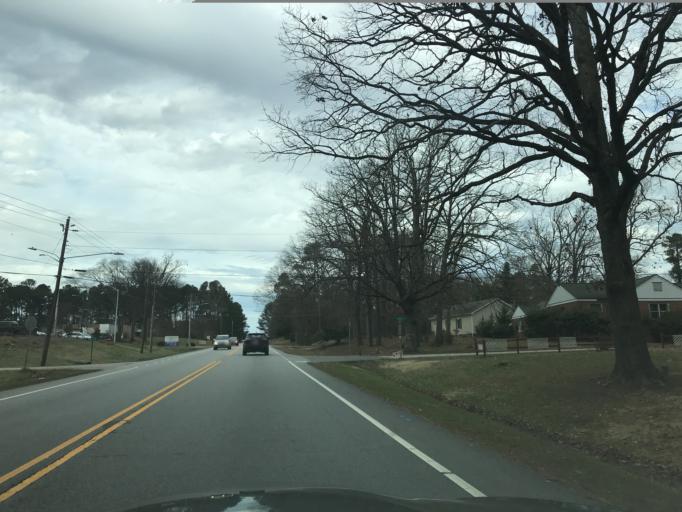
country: US
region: North Carolina
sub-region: Franklin County
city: Louisburg
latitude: 36.1116
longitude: -78.2922
